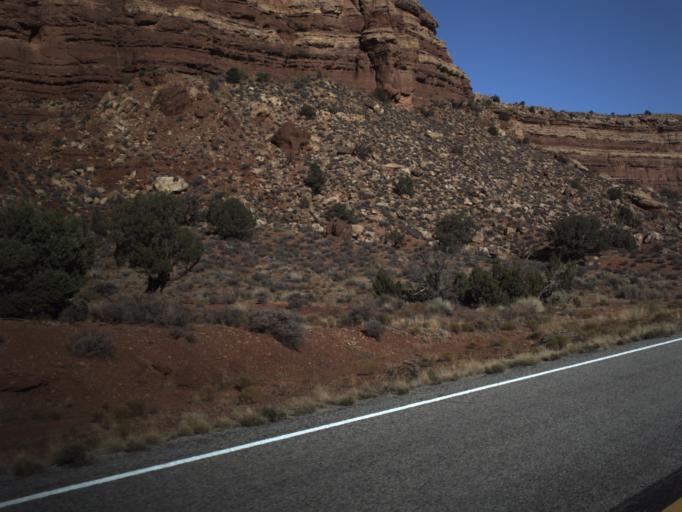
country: US
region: Utah
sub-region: San Juan County
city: Blanding
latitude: 37.7243
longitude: -110.2494
